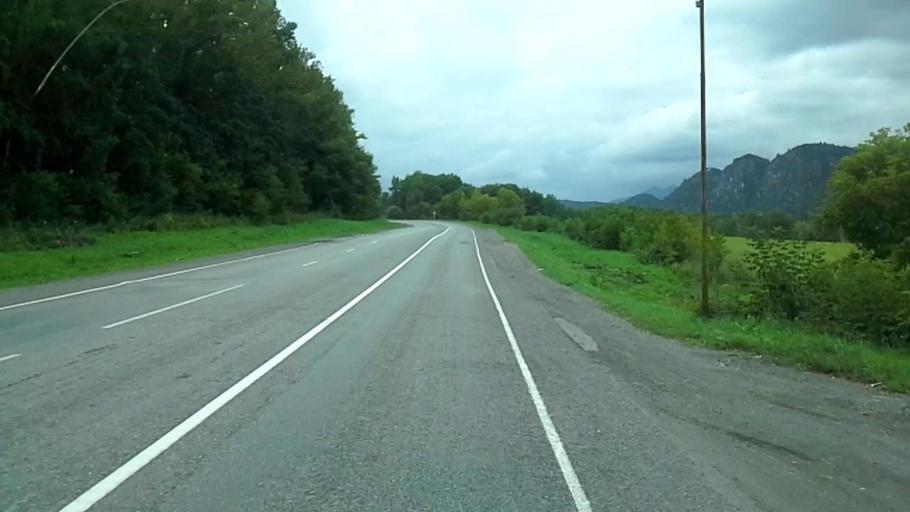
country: RU
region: Altay
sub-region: Mayminskiy Rayon
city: Manzherok
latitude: 51.8636
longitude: 85.7632
